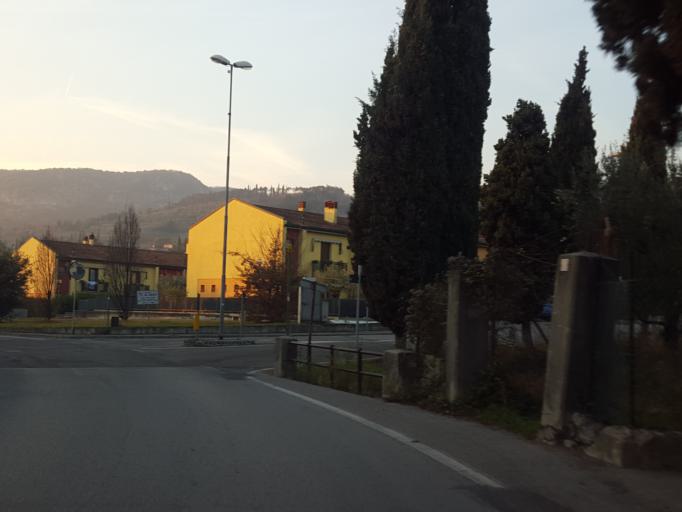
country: IT
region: Veneto
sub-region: Provincia di Verona
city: Garda
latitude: 45.5802
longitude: 10.7171
